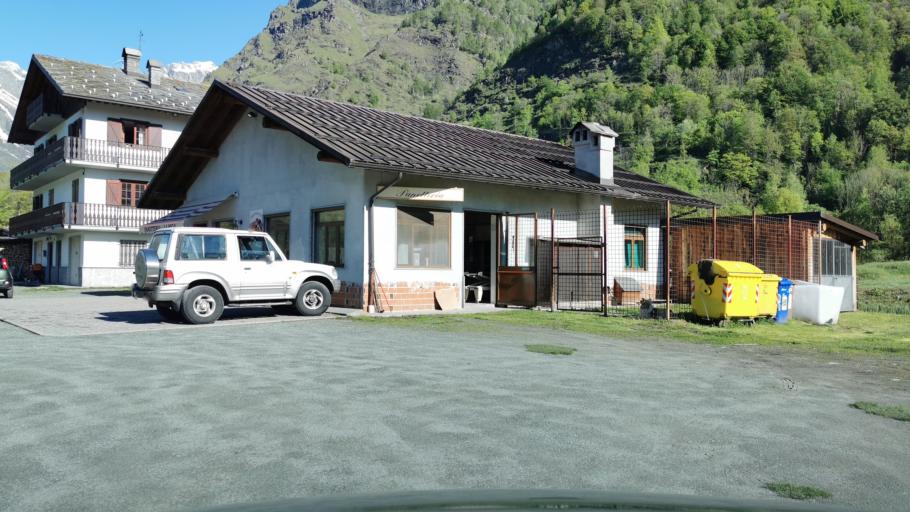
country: IT
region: Piedmont
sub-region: Provincia di Torino
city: Usseglio
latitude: 45.2322
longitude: 7.2343
